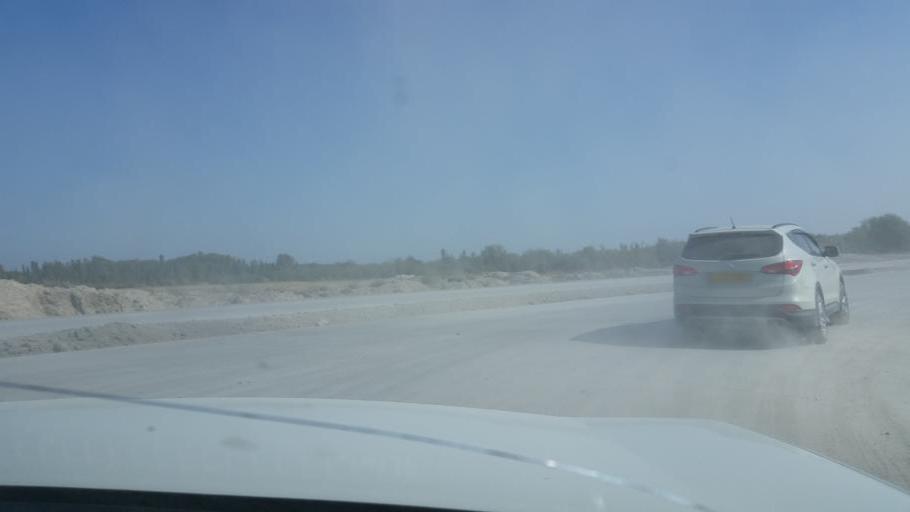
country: KZ
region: Almaty Oblysy
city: Turgen'
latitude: 43.5285
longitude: 77.5650
